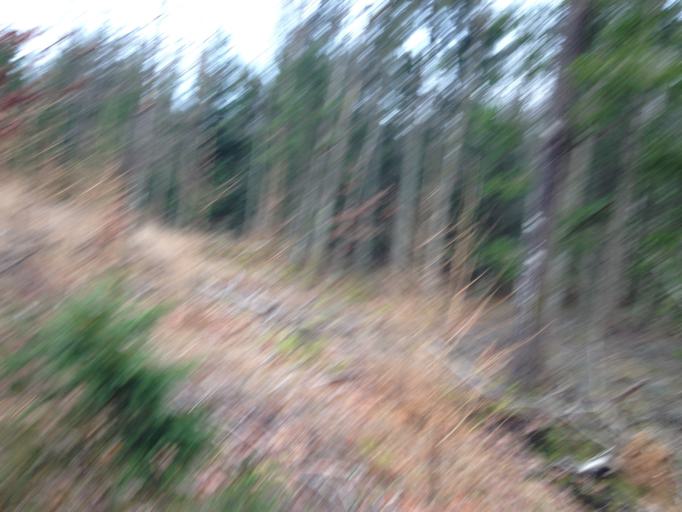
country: SE
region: Joenkoeping
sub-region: Varnamo Kommun
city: Bor
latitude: 57.0362
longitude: 14.1880
